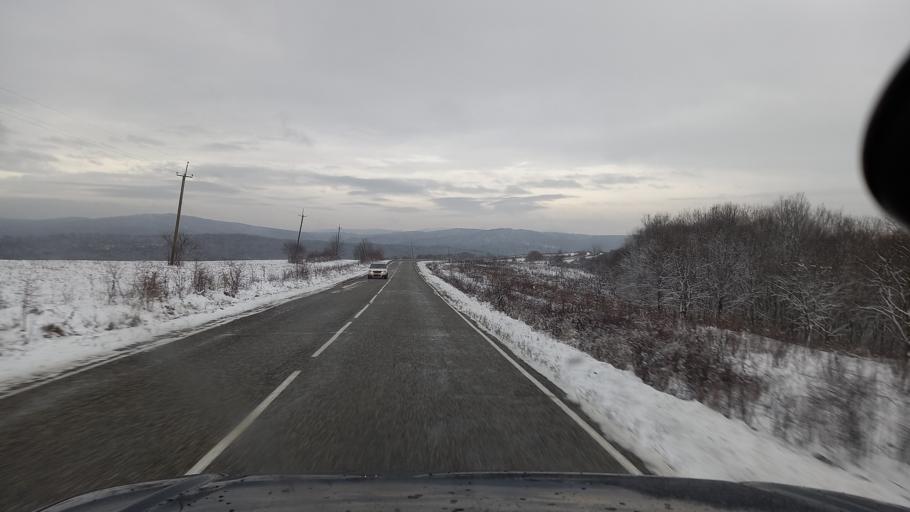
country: RU
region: Adygeya
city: Abadzekhskaya
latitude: 44.3584
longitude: 40.3750
